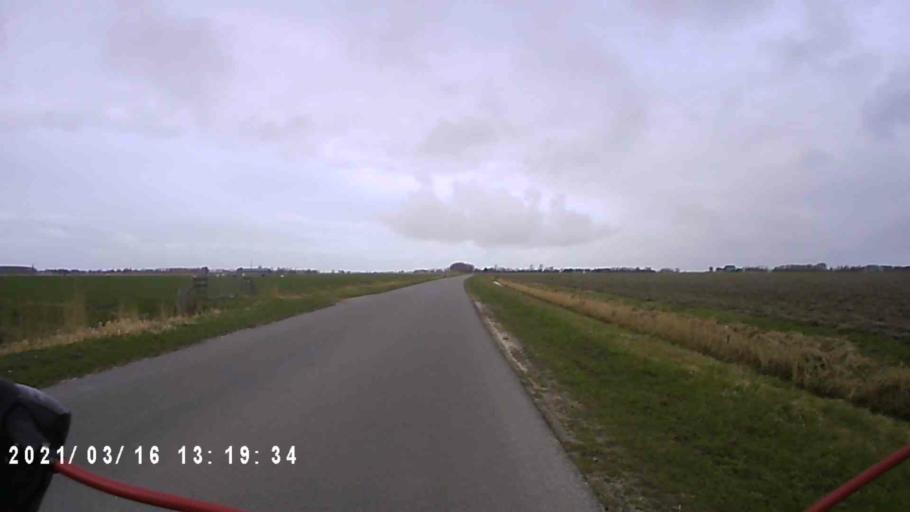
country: NL
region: Friesland
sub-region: Gemeente Het Bildt
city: Minnertsga
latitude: 53.2346
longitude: 5.5821
